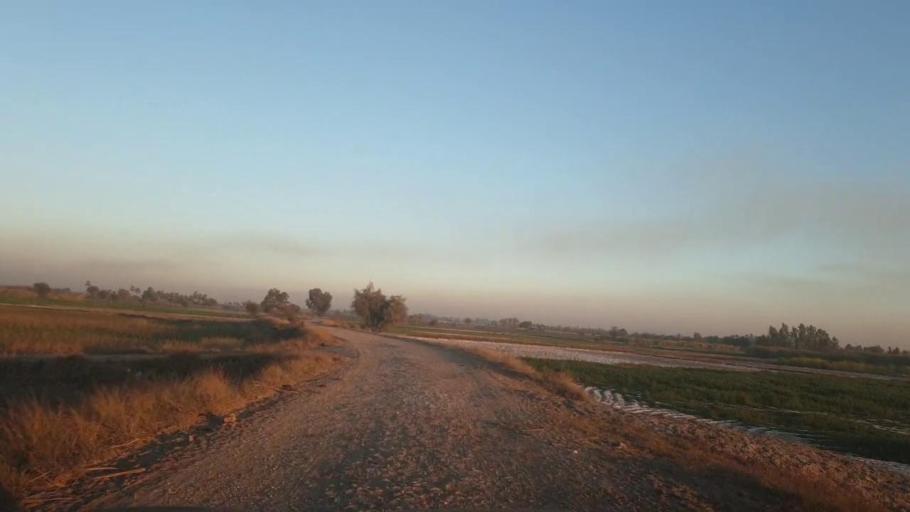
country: PK
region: Sindh
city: Ghotki
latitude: 28.0344
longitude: 69.3017
